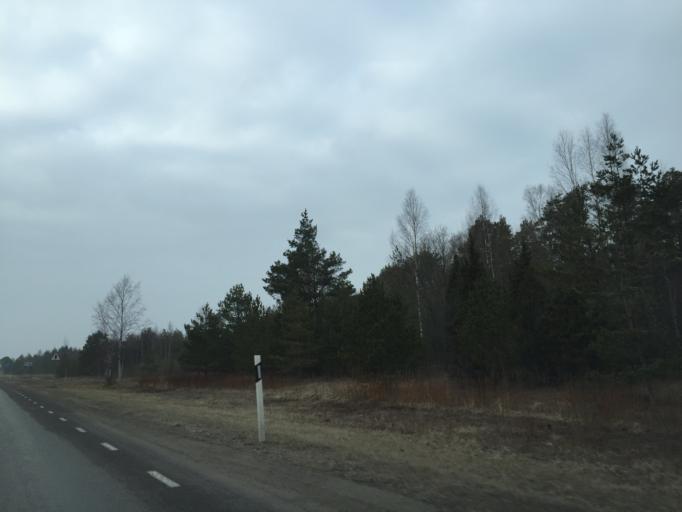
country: EE
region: Saare
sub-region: Orissaare vald
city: Orissaare
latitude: 58.5749
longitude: 23.3744
